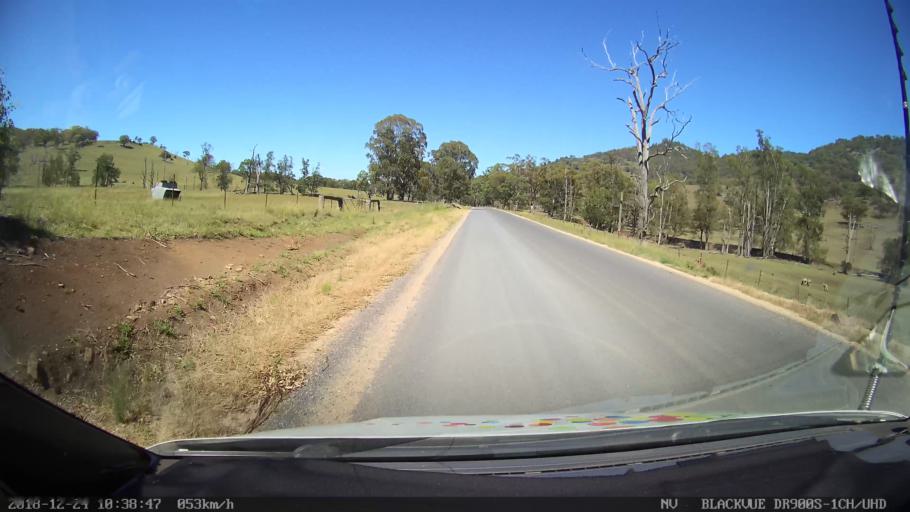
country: AU
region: New South Wales
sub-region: Upper Hunter Shire
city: Merriwa
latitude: -31.8496
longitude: 150.4799
